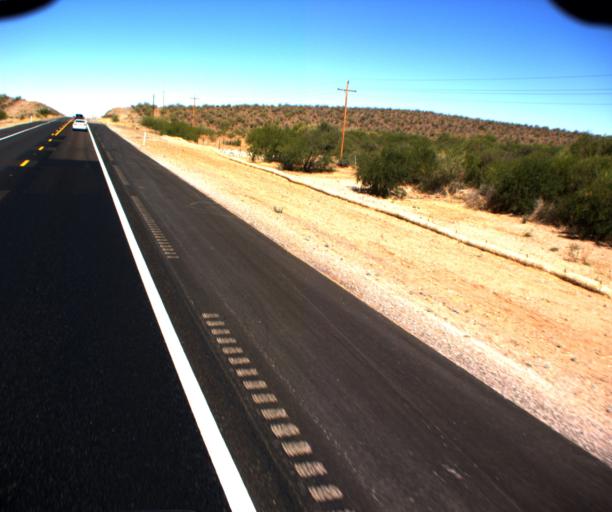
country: US
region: Arizona
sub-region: Pima County
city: Sells
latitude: 31.9168
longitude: -111.8501
